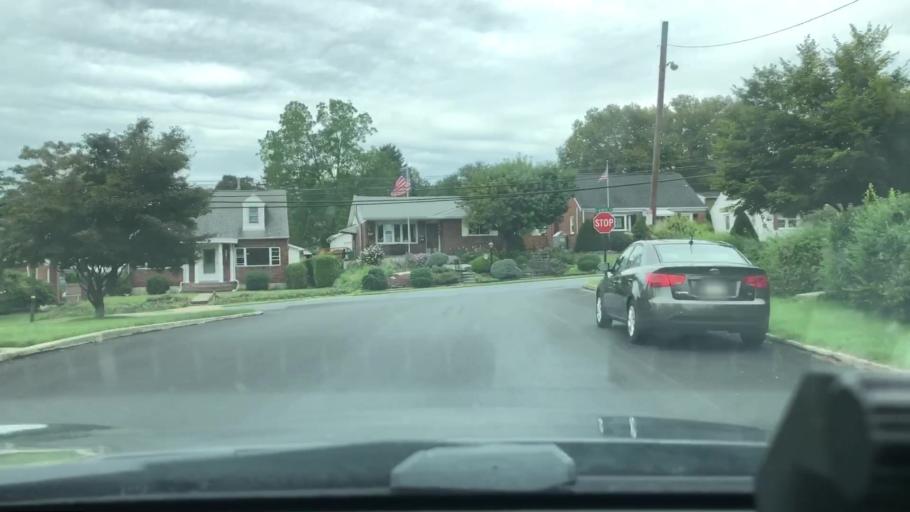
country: US
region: Pennsylvania
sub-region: Lehigh County
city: Dorneyville
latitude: 40.5857
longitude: -75.5032
